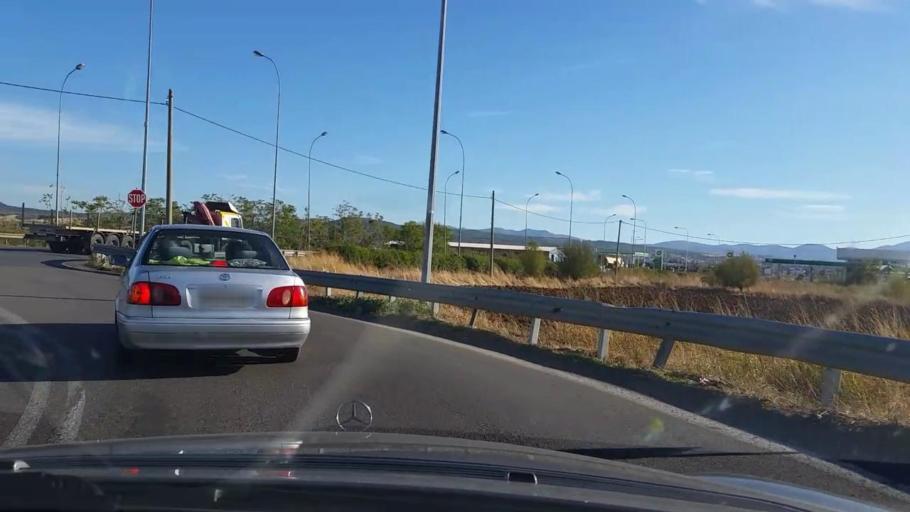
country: GR
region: Central Greece
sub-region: Nomos Voiotias
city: Thivai
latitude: 38.3619
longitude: 23.3222
